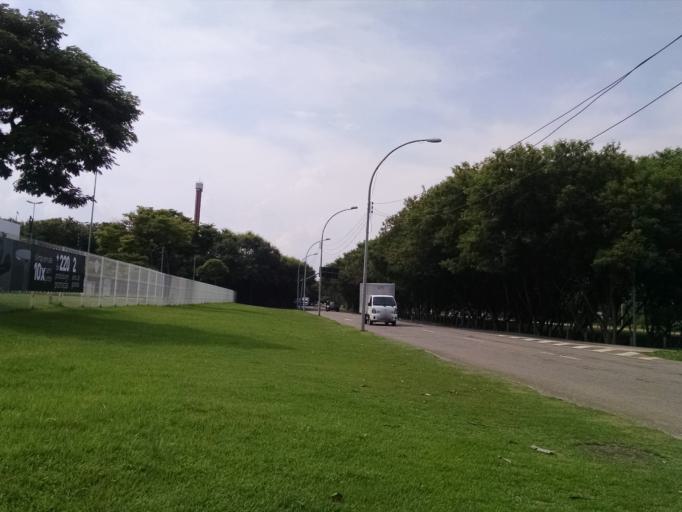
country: BR
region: Rio de Janeiro
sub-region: Rio De Janeiro
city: Rio de Janeiro
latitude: -22.9914
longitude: -43.3614
